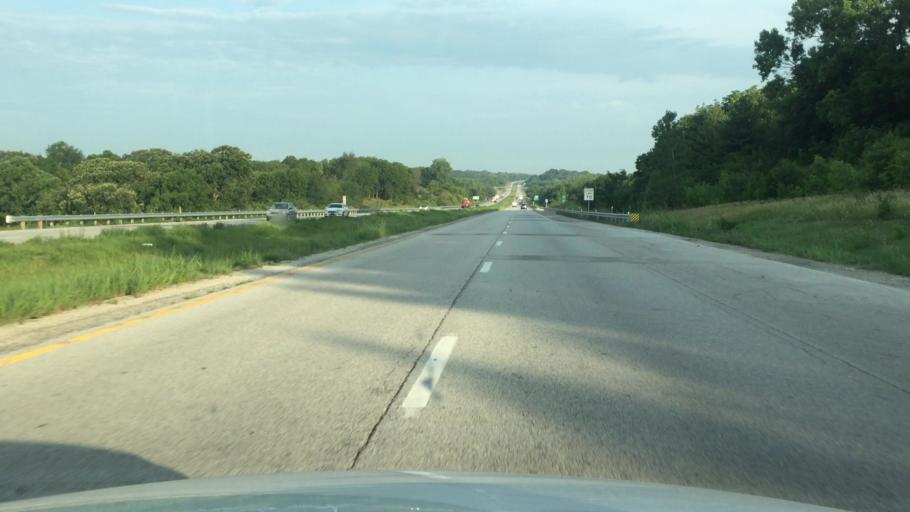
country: US
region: Missouri
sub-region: Buchanan County
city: Saint Joseph
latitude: 39.7114
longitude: -94.8009
